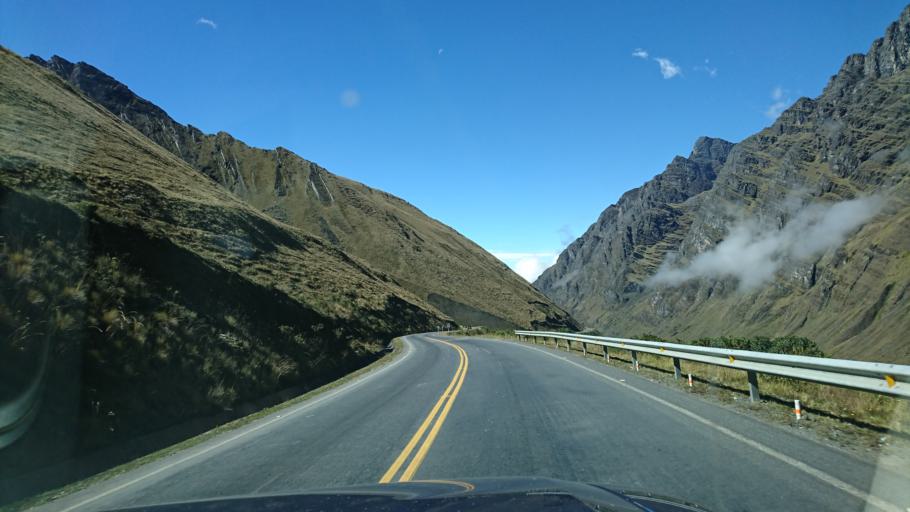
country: BO
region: La Paz
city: La Paz
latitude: -16.3302
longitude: -67.9605
